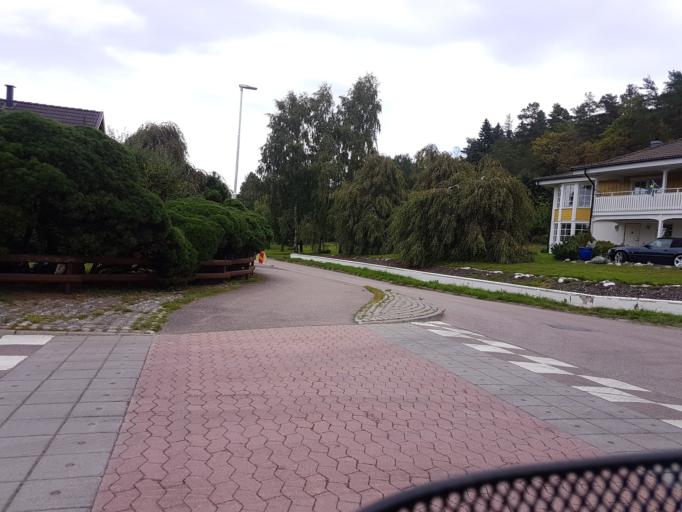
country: SE
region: Vaestra Goetaland
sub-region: Ale Kommun
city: Nodinge-Nol
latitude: 57.8956
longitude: 12.0554
